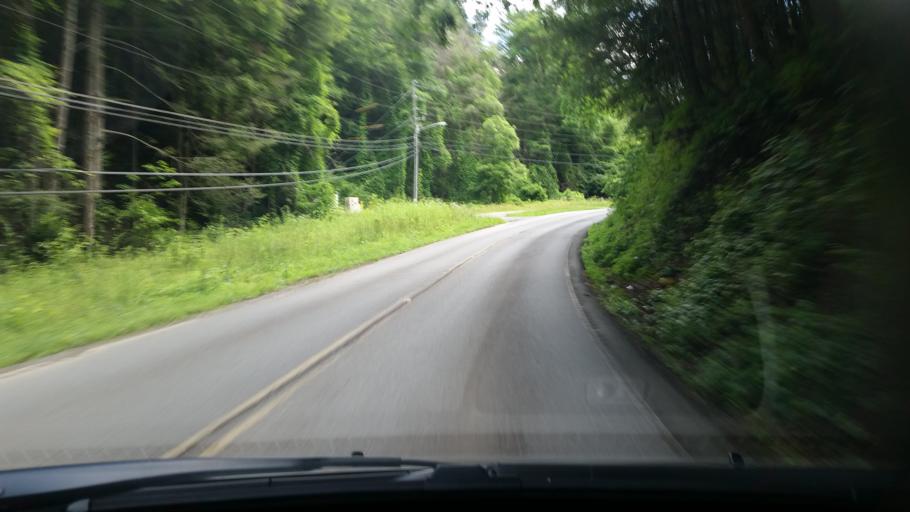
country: US
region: Tennessee
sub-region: Sevier County
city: Gatlinburg
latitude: 35.7385
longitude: -83.4662
